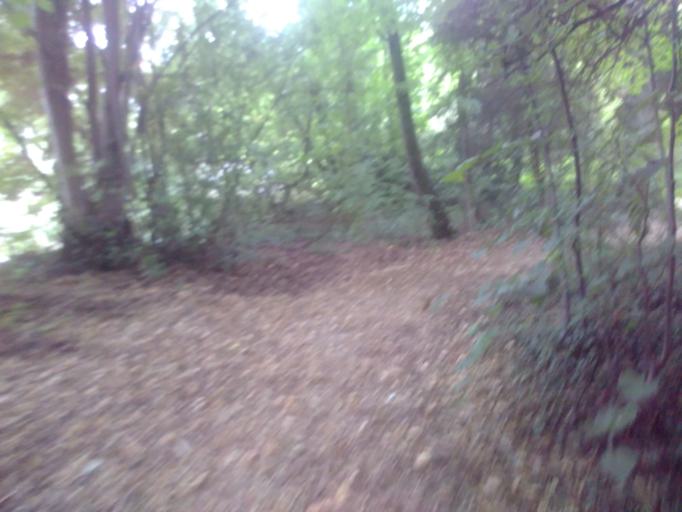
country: FR
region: Rhone-Alpes
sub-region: Departement de l'Isere
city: La Tronche
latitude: 45.2059
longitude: 5.7539
